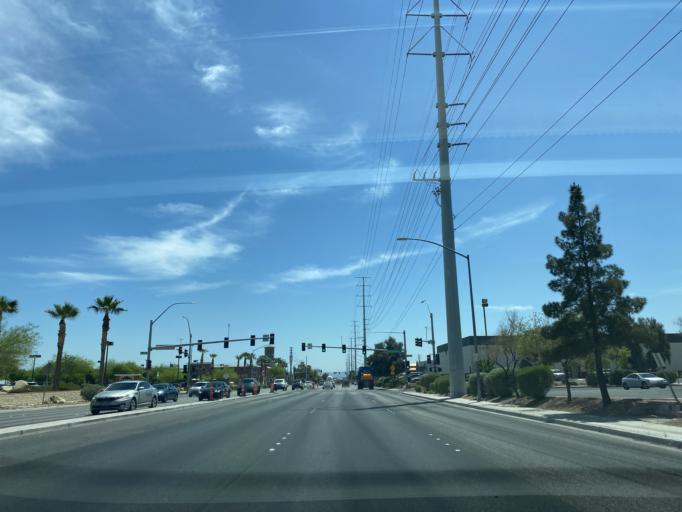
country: US
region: Nevada
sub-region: Clark County
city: North Las Vegas
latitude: 36.2426
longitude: -115.1169
